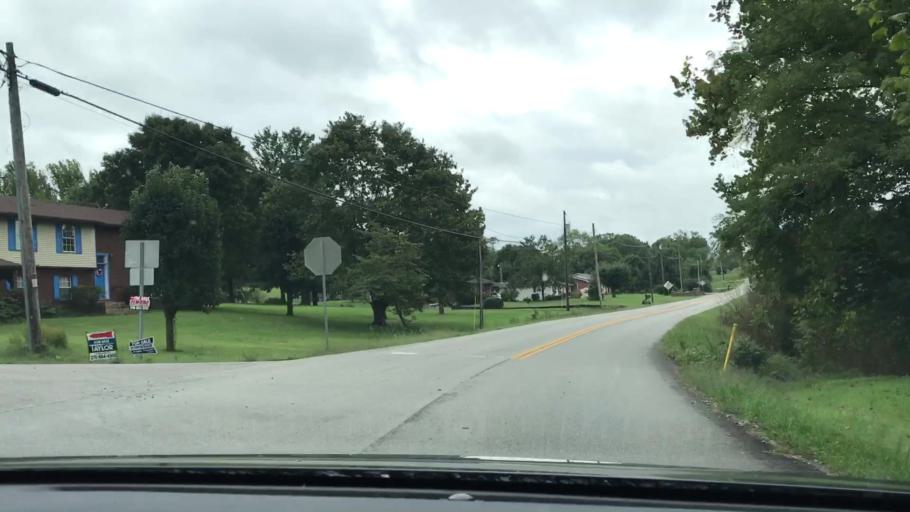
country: US
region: Kentucky
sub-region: Barren County
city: Glasgow
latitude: 36.9622
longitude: -85.8663
